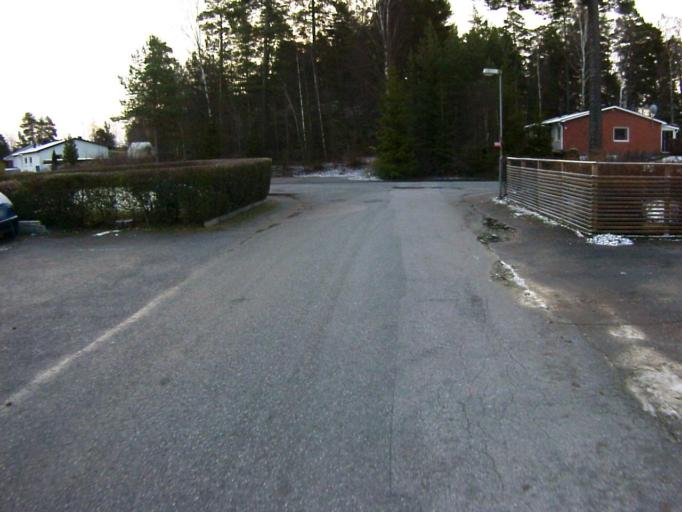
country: SE
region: Soedermanland
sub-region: Eskilstuna Kommun
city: Hallbybrunn
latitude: 59.3971
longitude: 16.4163
